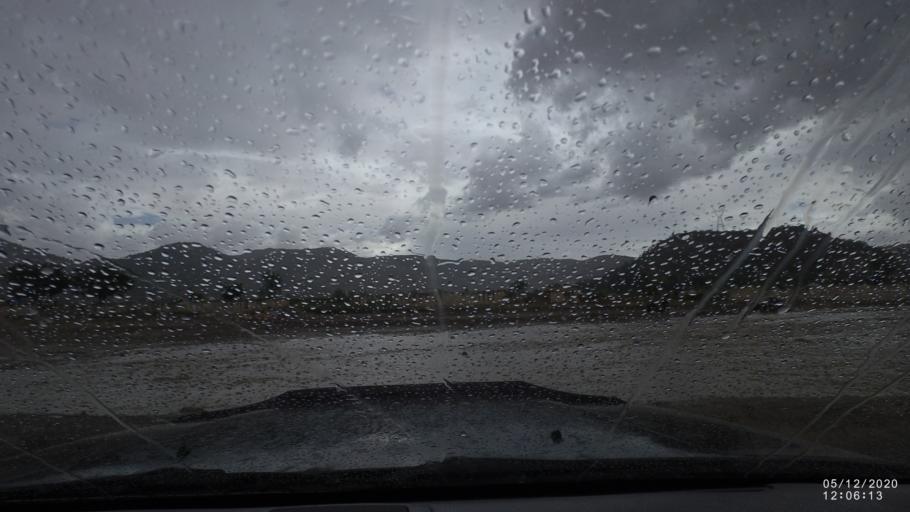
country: BO
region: Cochabamba
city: Sipe Sipe
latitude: -17.5724
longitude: -66.3611
